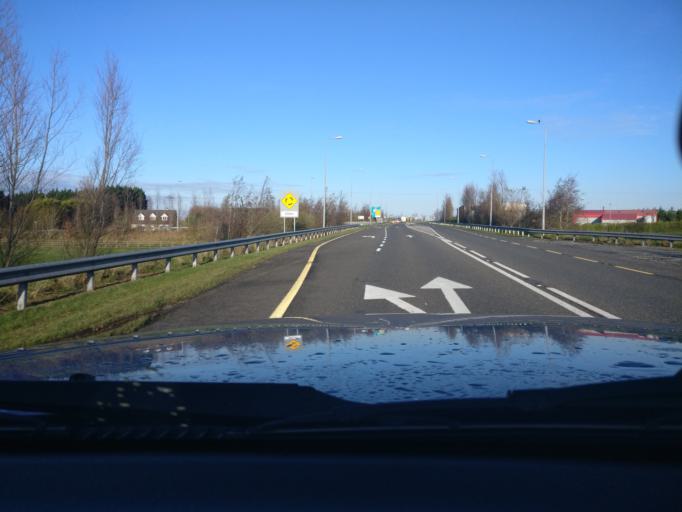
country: IE
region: Connaught
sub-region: County Galway
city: Loughrea
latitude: 53.2619
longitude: -8.6078
